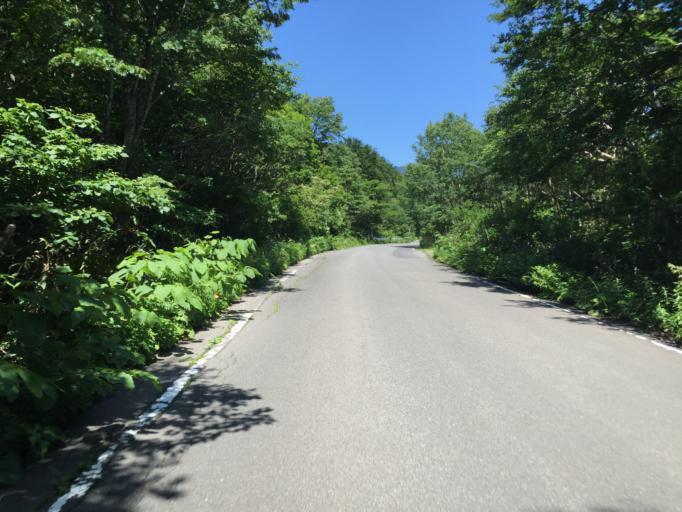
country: JP
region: Fukushima
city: Nihommatsu
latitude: 37.6593
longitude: 140.2865
